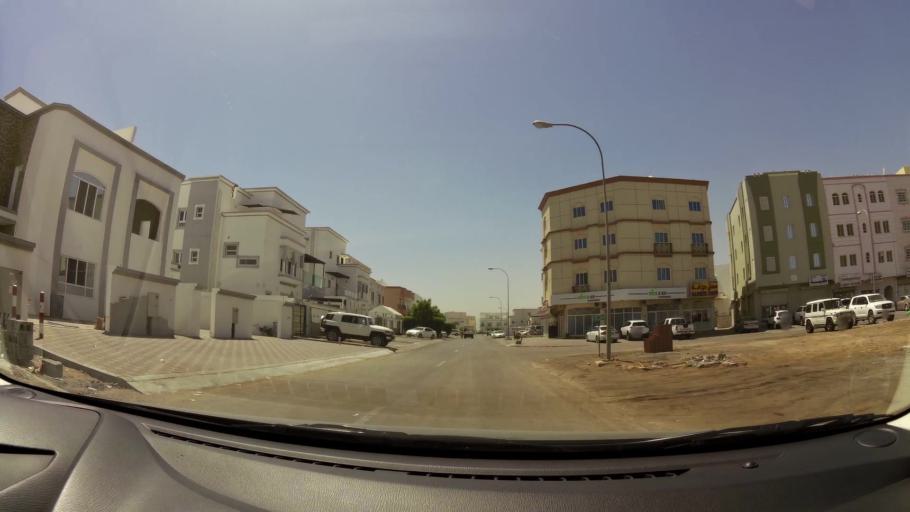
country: OM
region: Muhafazat Masqat
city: As Sib al Jadidah
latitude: 23.6250
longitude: 58.2559
